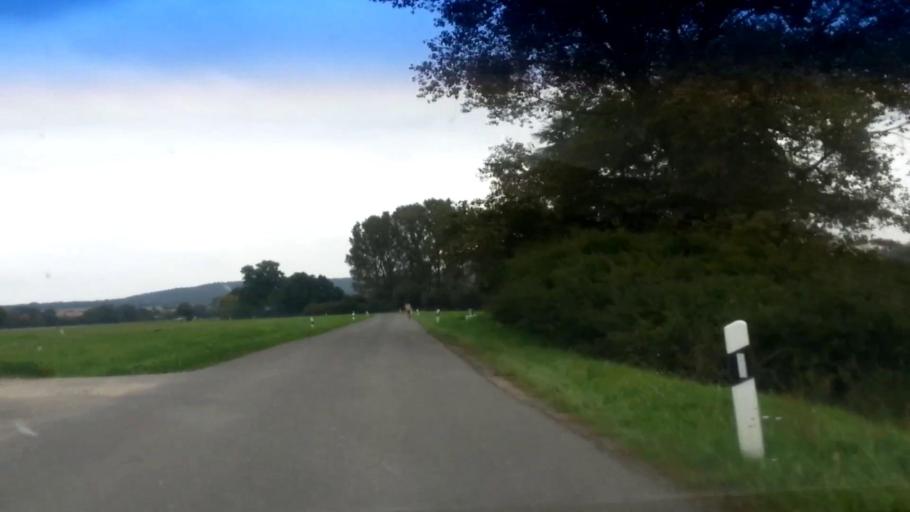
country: DE
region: Bavaria
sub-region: Upper Franconia
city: Rattelsdorf
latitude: 50.0157
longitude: 10.9091
